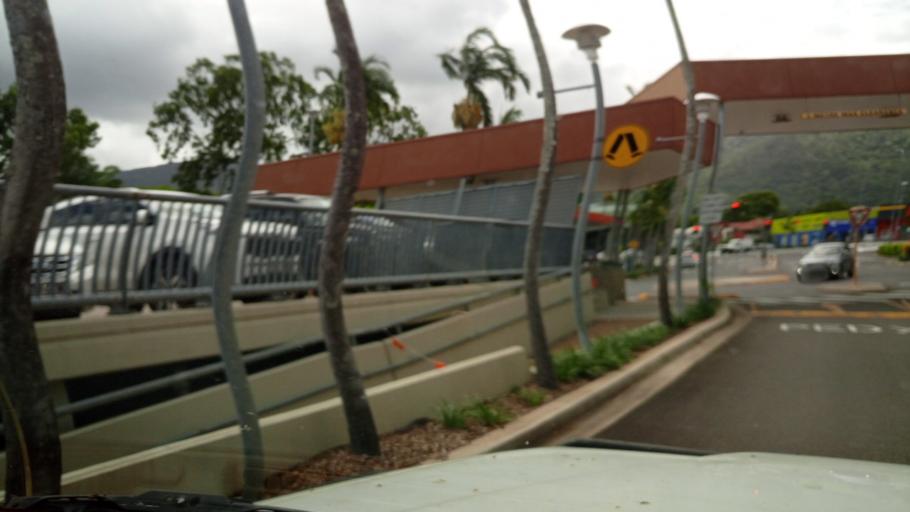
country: AU
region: Queensland
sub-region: Cairns
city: Woree
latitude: -16.9454
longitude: 145.7393
